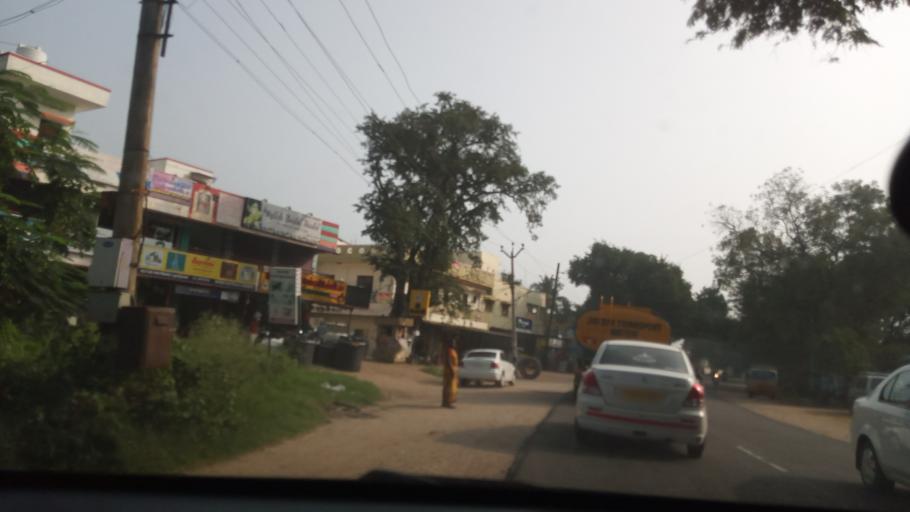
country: IN
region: Tamil Nadu
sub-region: Coimbatore
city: Periyanayakkanpalaiyam
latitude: 11.1421
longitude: 77.0376
